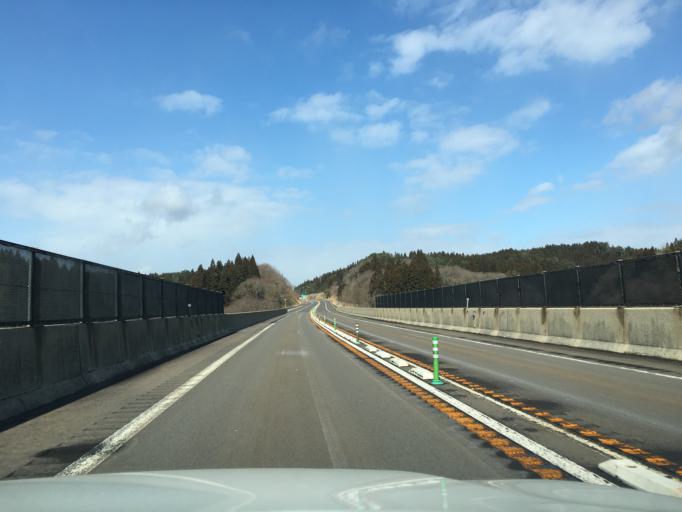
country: JP
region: Akita
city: Akita
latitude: 39.7446
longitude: 140.1599
